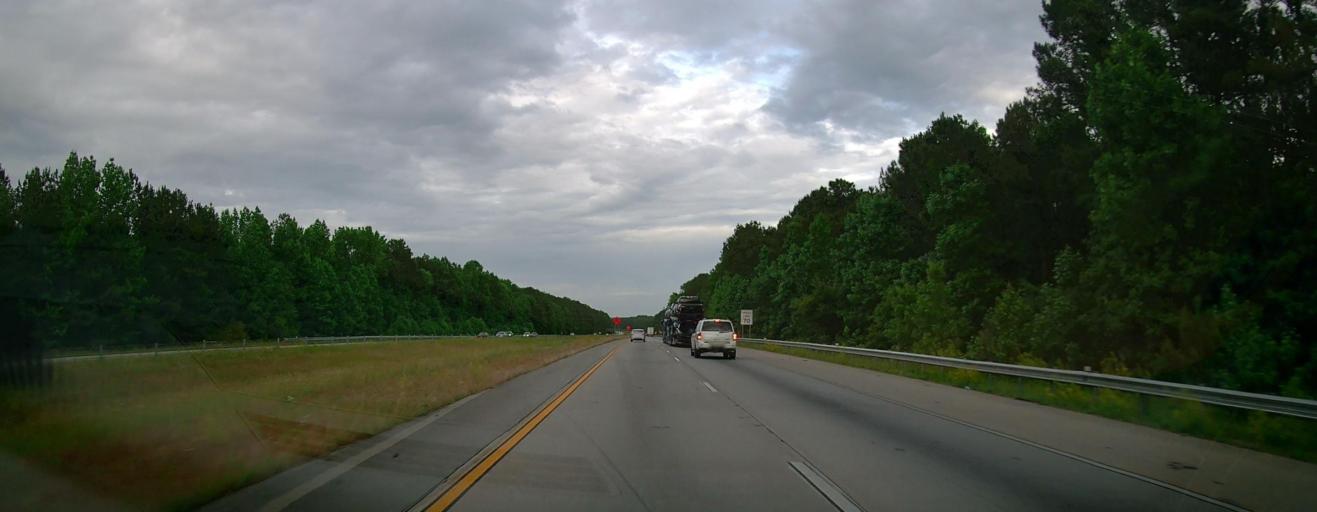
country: US
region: Georgia
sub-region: Haralson County
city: Bremen
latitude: 33.6852
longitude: -85.1427
